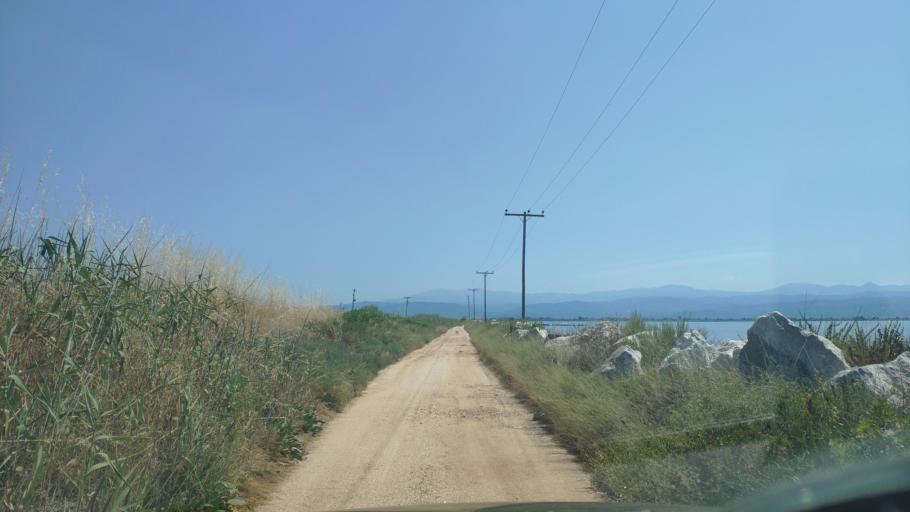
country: GR
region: Epirus
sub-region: Nomos Artas
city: Aneza
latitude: 39.0247
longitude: 20.9384
